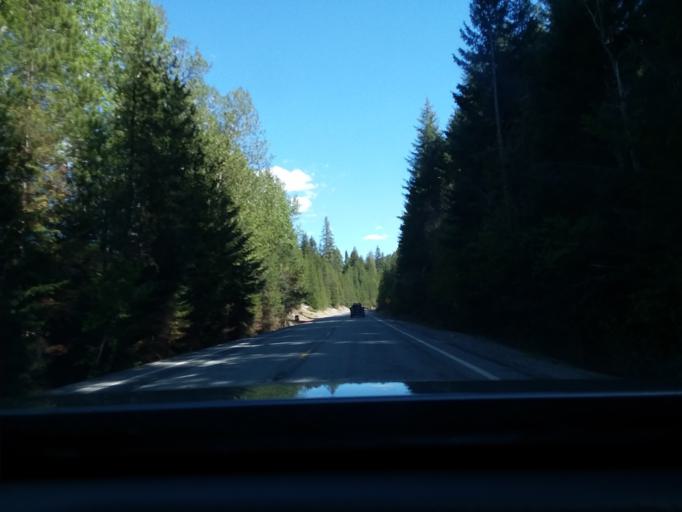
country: US
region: Washington
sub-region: Chelan County
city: Leavenworth
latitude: 47.7966
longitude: -120.6659
